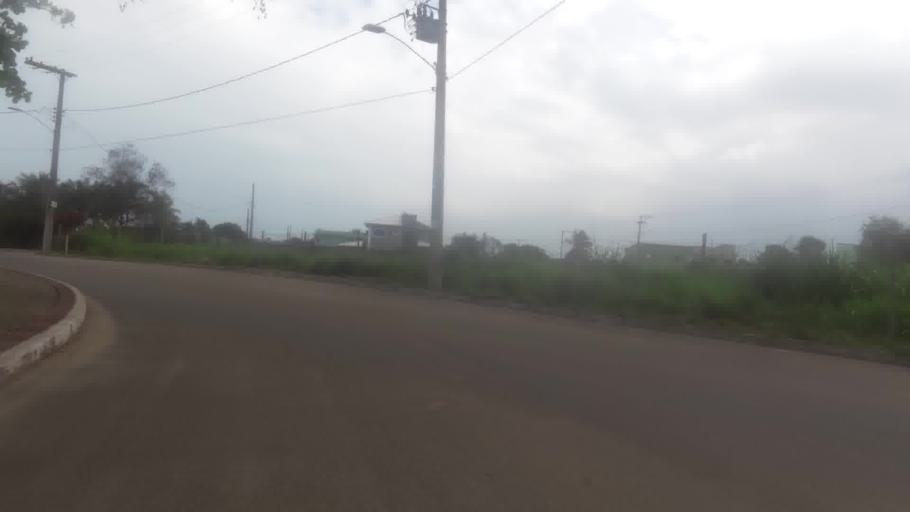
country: BR
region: Espirito Santo
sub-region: Piuma
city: Piuma
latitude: -20.7980
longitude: -40.5869
